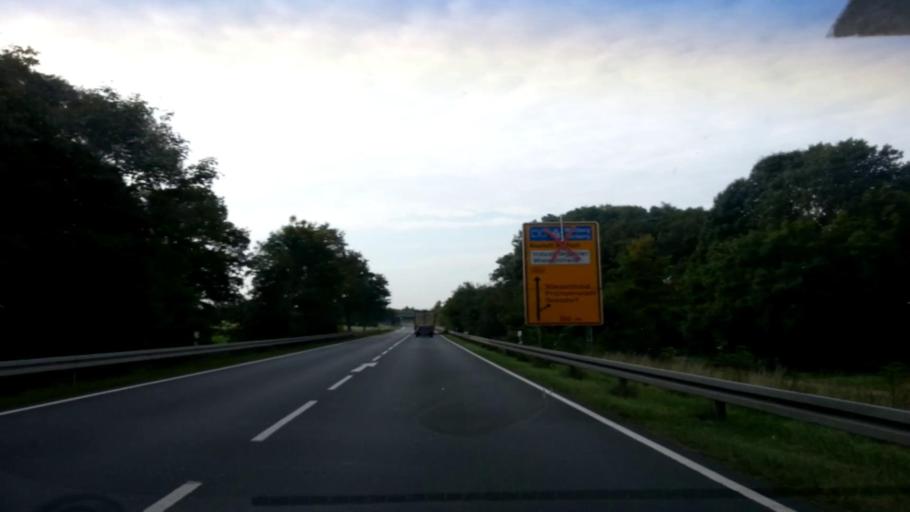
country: DE
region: Bavaria
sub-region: Regierungsbezirk Unterfranken
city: Wiesentheid
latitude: 49.8016
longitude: 10.3588
